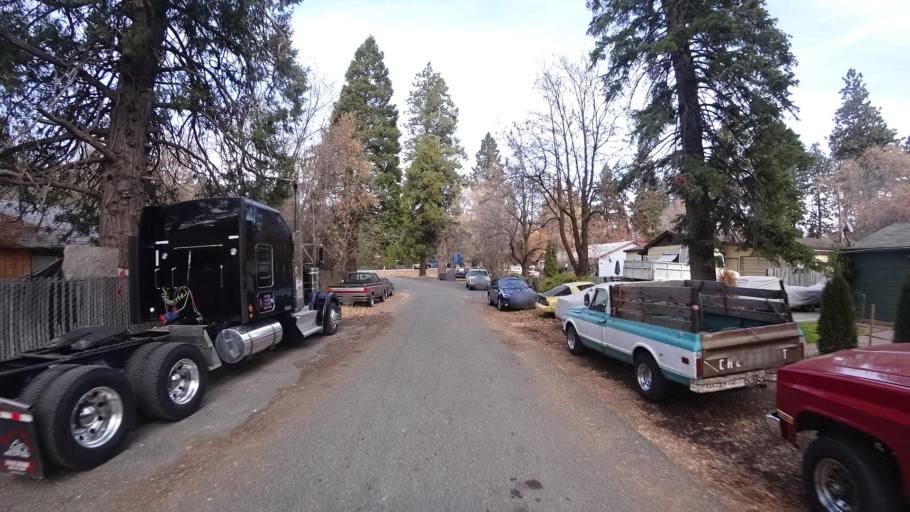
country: US
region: California
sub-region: Siskiyou County
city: Weed
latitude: 41.4480
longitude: -122.3634
